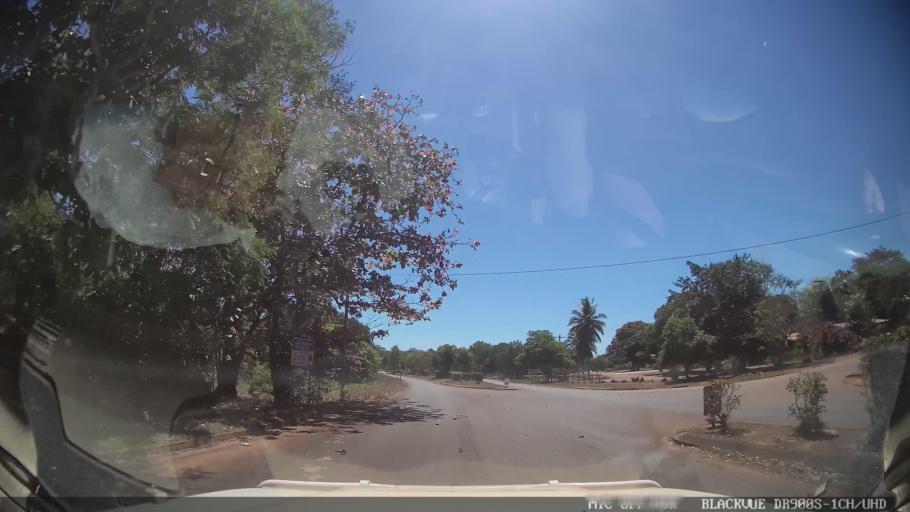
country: AU
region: Queensland
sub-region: Torres
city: Thursday Island
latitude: -10.8842
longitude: 142.3882
